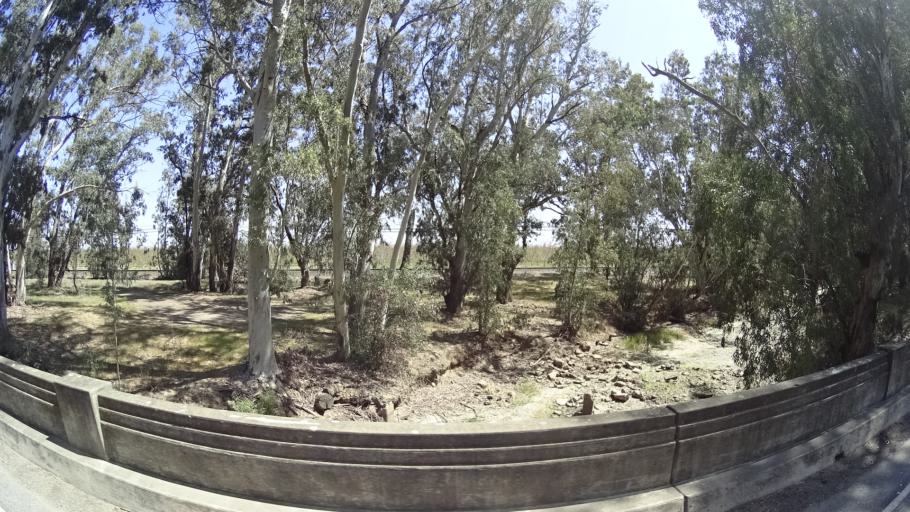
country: US
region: California
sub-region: Glenn County
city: Willows
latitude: 39.5947
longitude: -122.1944
